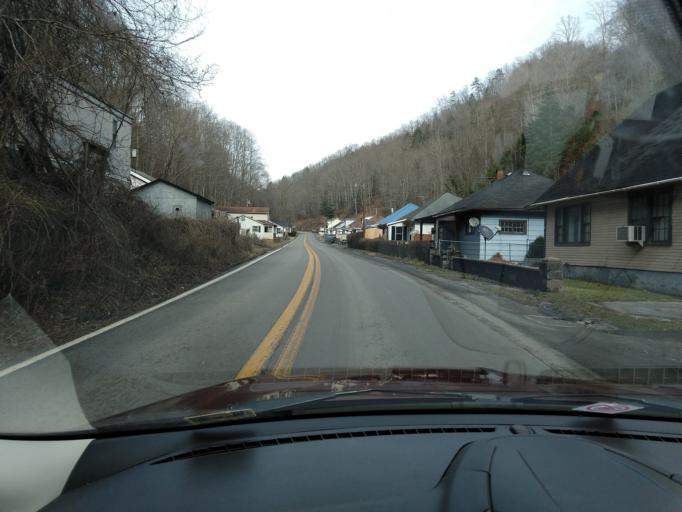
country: US
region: West Virginia
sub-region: McDowell County
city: Welch
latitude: 37.3353
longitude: -81.6735
